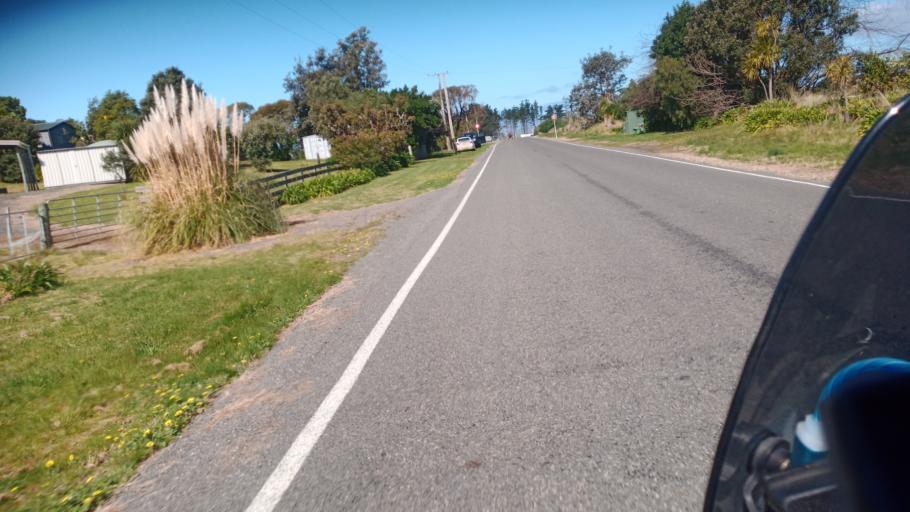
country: NZ
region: Gisborne
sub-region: Gisborne District
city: Gisborne
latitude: -39.0166
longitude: 177.8811
